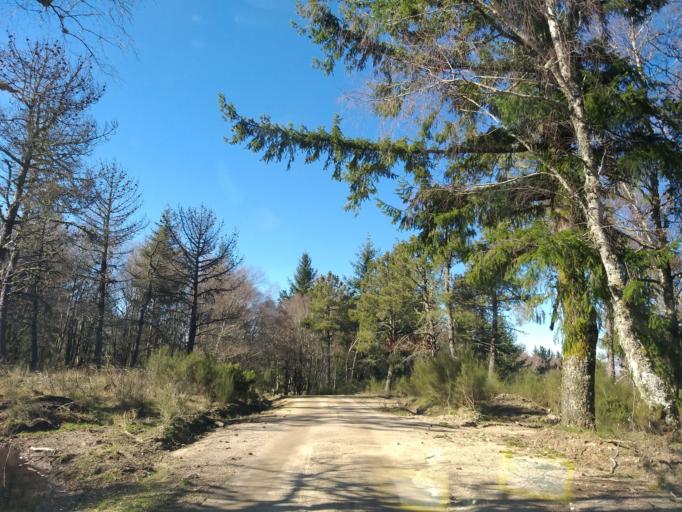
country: PT
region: Guarda
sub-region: Manteigas
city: Manteigas
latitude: 40.4901
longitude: -7.4923
